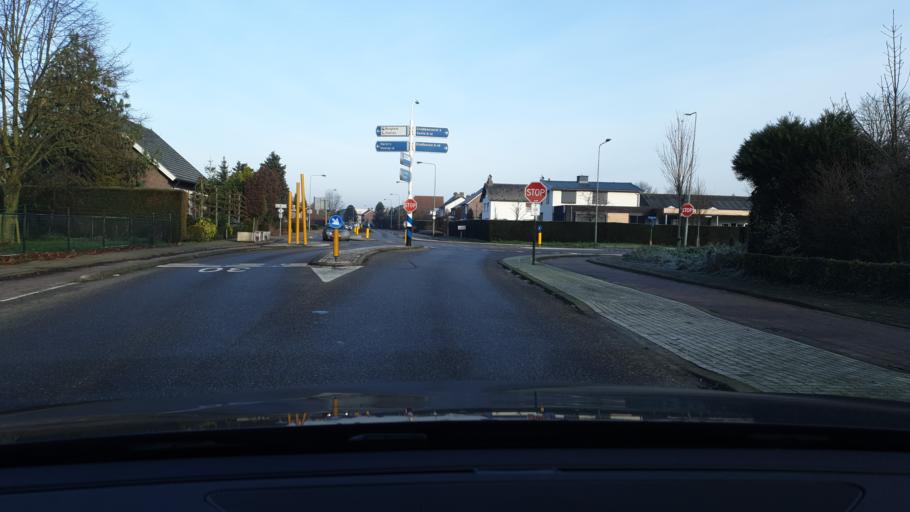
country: NL
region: Limburg
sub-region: Gemeente Peel en Maas
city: Maasbree
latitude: 51.4169
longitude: 6.0350
